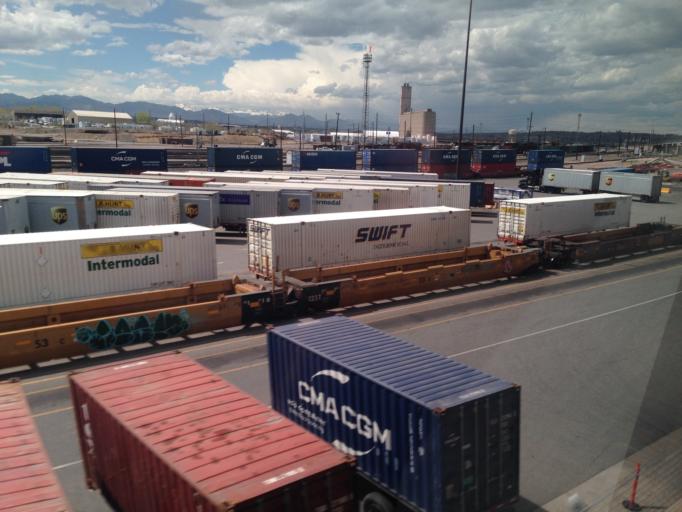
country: US
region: Colorado
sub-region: Adams County
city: Twin Lakes
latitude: 39.7966
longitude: -104.9964
